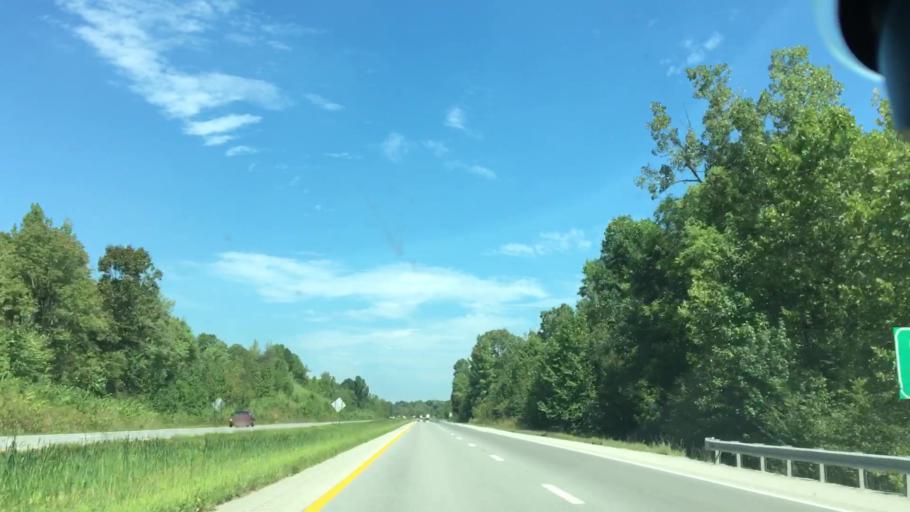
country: US
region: Kentucky
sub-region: Hopkins County
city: Nortonville
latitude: 37.1638
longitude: -87.4556
